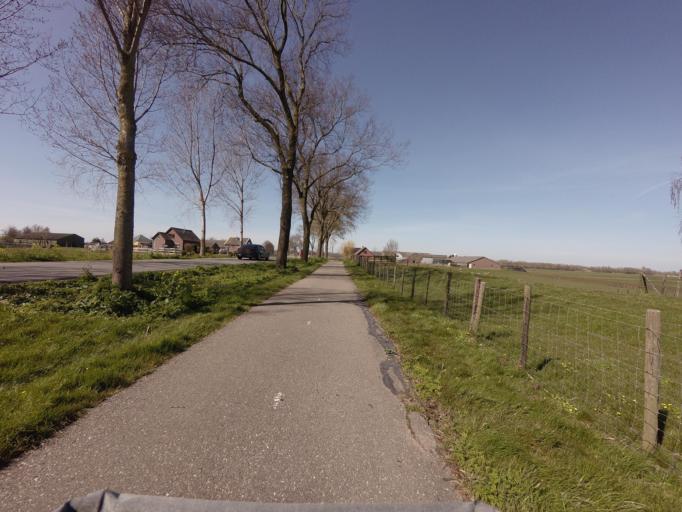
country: NL
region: Utrecht
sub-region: Gemeente De Ronde Venen
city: Mijdrecht
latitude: 52.1770
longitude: 4.8974
